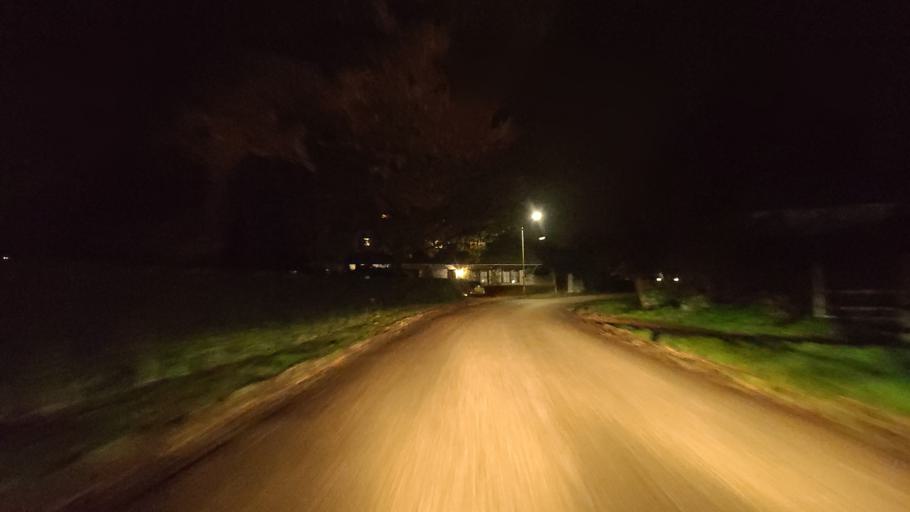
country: NL
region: Limburg
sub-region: Gemeente Gennep
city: Gennep
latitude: 51.7217
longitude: 5.9608
